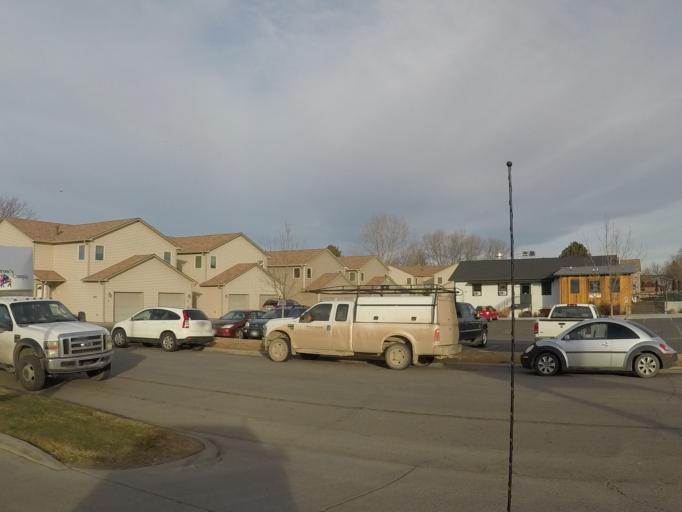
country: US
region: Montana
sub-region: Yellowstone County
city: Billings
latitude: 45.7569
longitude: -108.5972
